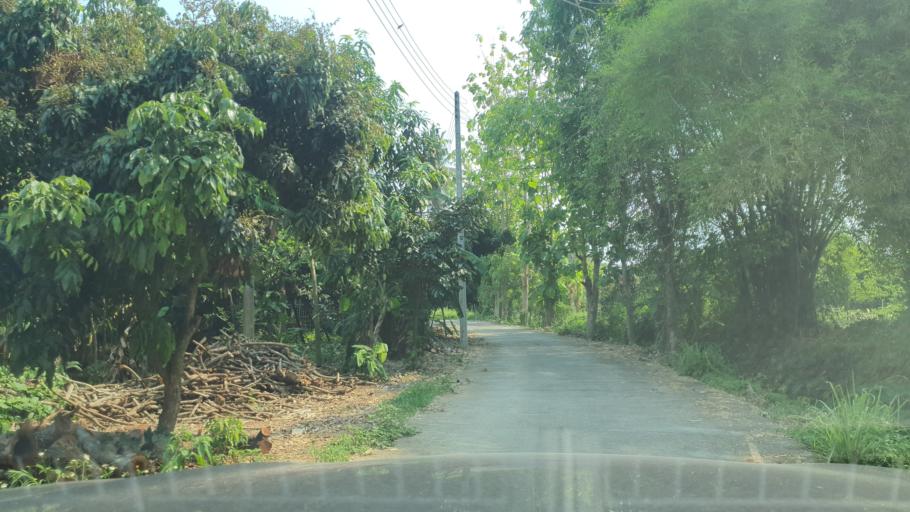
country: TH
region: Chiang Mai
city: Saraphi
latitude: 18.6559
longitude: 98.9880
